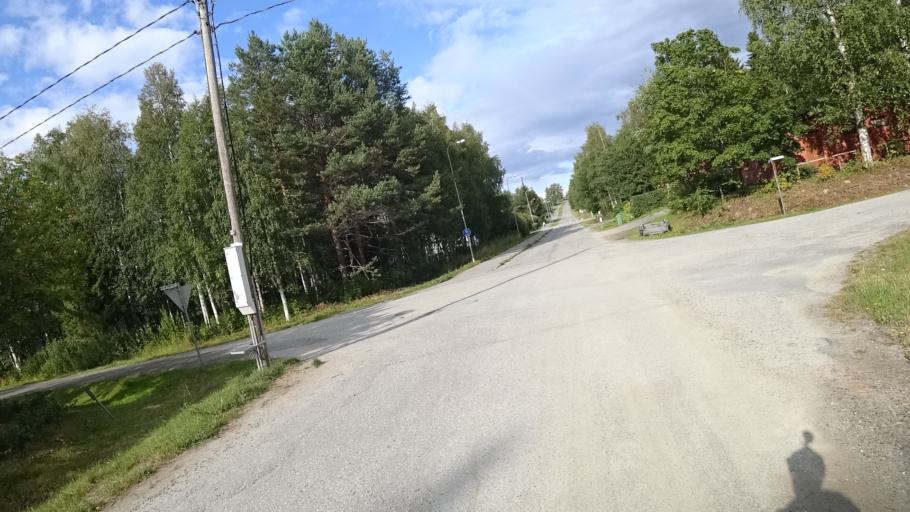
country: FI
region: North Karelia
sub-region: Joensuu
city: Ilomantsi
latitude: 62.6662
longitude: 30.9145
